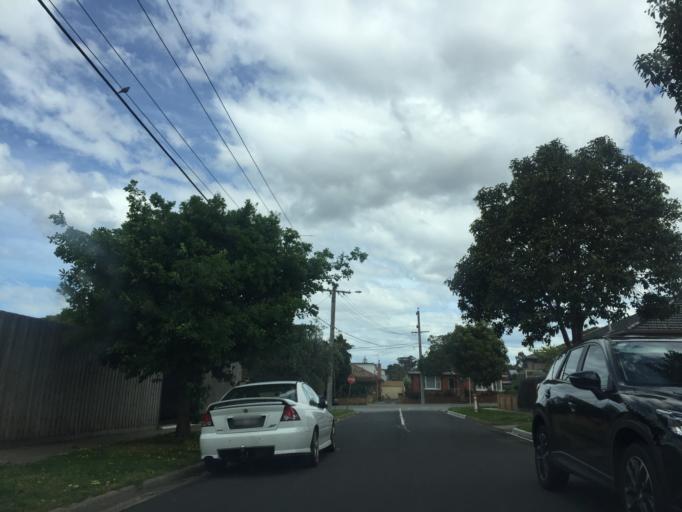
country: AU
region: Victoria
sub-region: Darebin
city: Preston
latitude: -37.7495
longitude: 145.0128
